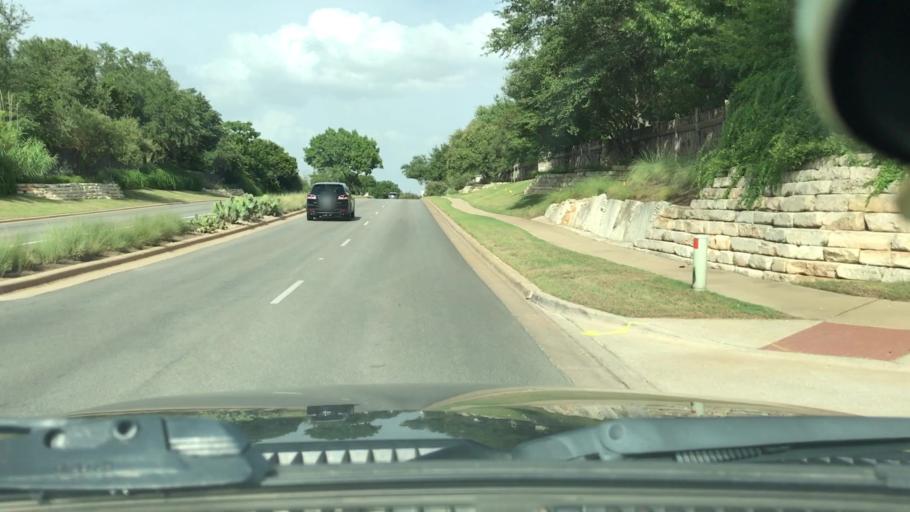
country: US
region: Texas
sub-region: Williamson County
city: Leander
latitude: 30.5462
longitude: -97.8616
